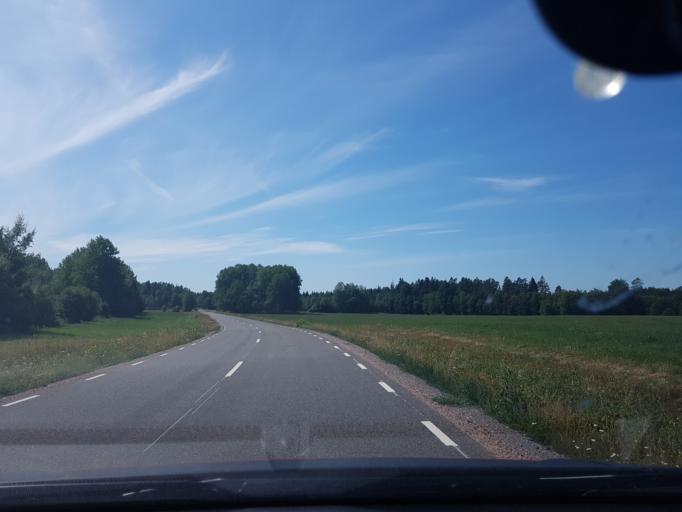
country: SE
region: Joenkoeping
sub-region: Gislaveds Kommun
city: Reftele
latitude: 57.2060
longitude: 13.6006
